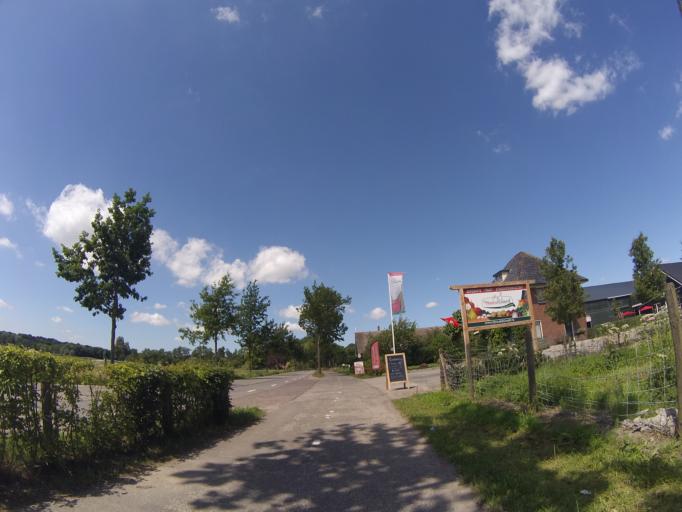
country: NL
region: Utrecht
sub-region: Stichtse Vecht
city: Spechtenkamp
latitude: 52.1181
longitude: 5.0026
